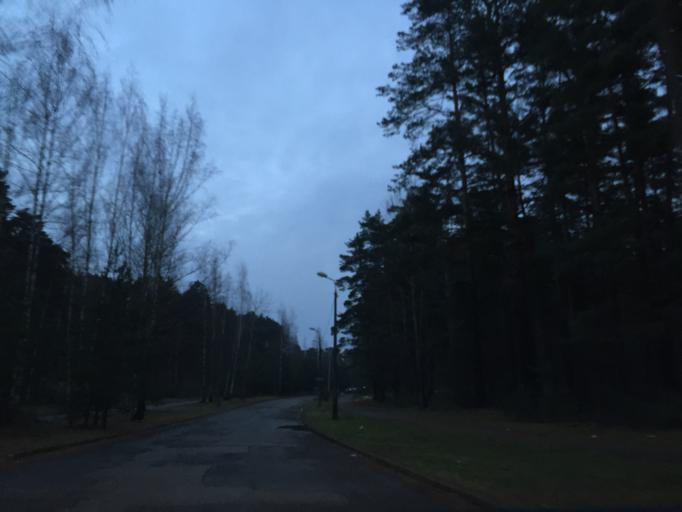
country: LV
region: Riga
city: Jaunciems
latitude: 57.0396
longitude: 24.1862
